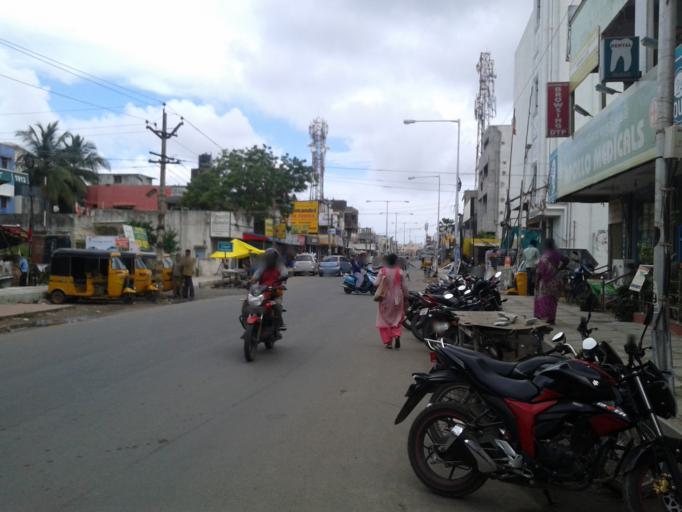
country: IN
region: Tamil Nadu
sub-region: Kancheepuram
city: Madipakkam
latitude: 12.9654
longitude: 80.2069
